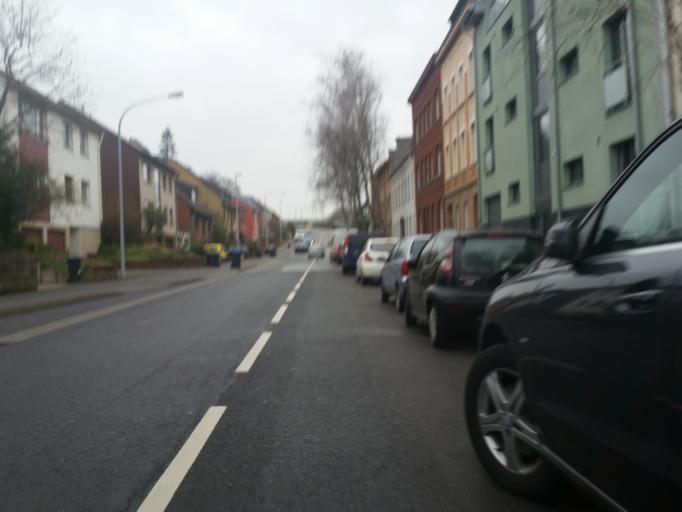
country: DE
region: North Rhine-Westphalia
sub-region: Regierungsbezirk Koln
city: Wurselen
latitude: 50.7959
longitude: 6.1307
